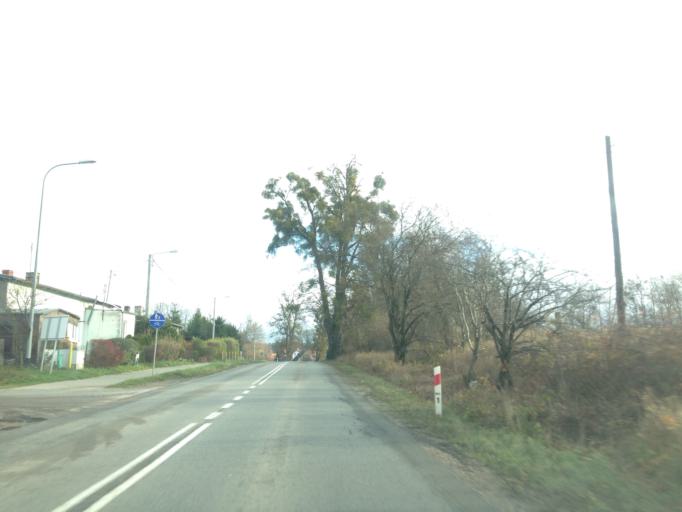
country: PL
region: Pomeranian Voivodeship
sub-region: Powiat gdanski
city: Lublewo Gdanskie
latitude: 54.2916
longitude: 18.5214
